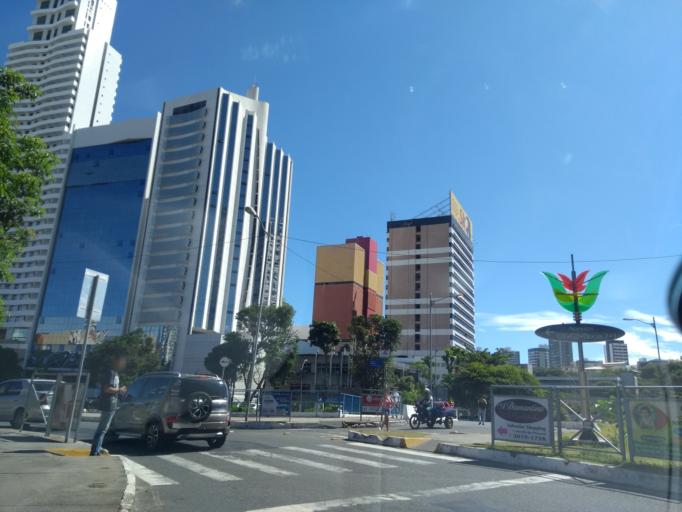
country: BR
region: Bahia
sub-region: Salvador
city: Salvador
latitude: -12.9778
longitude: -38.4571
